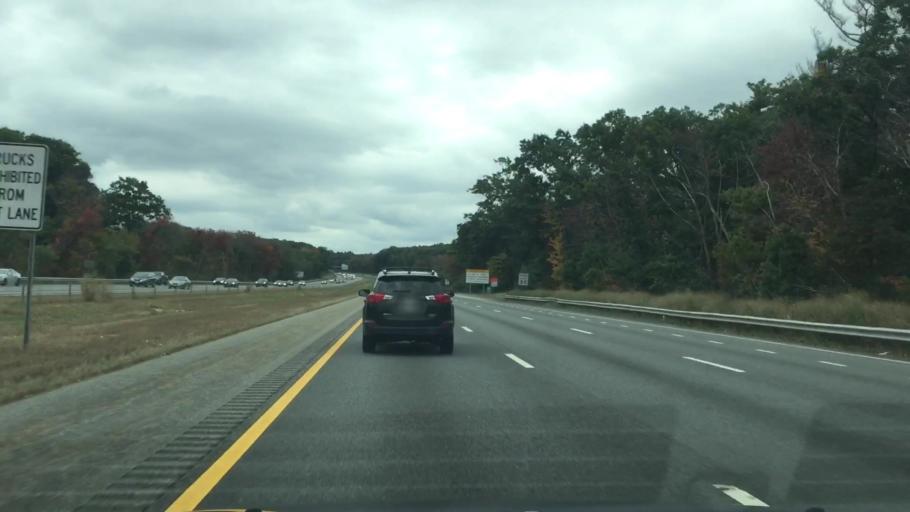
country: US
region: Massachusetts
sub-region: Middlesex County
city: Billerica
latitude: 42.5382
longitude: -71.2807
